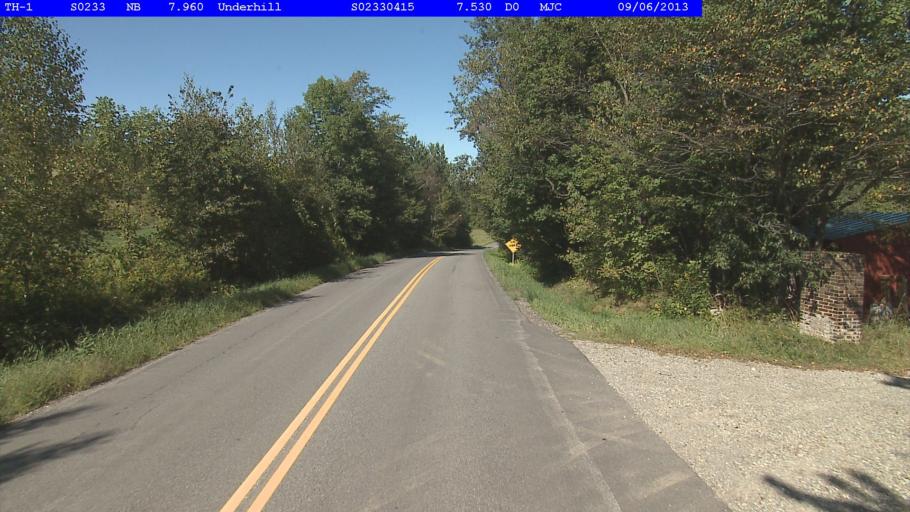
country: US
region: Vermont
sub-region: Chittenden County
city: Jericho
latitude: 44.5732
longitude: -72.8643
